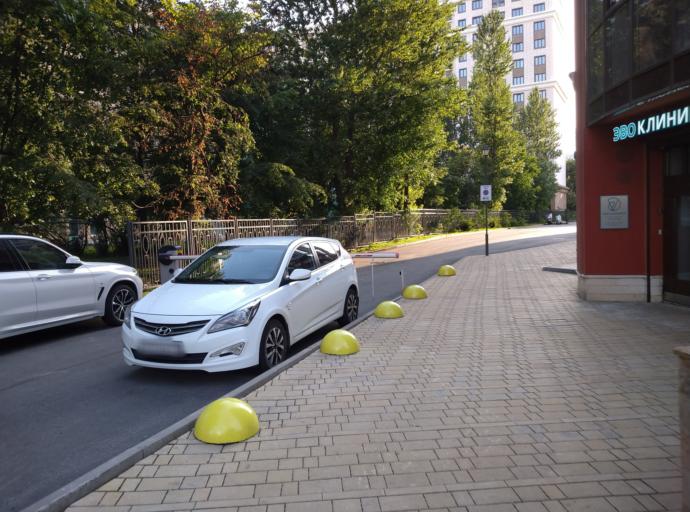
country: RU
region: St.-Petersburg
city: Saint Petersburg
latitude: 59.9056
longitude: 30.3250
